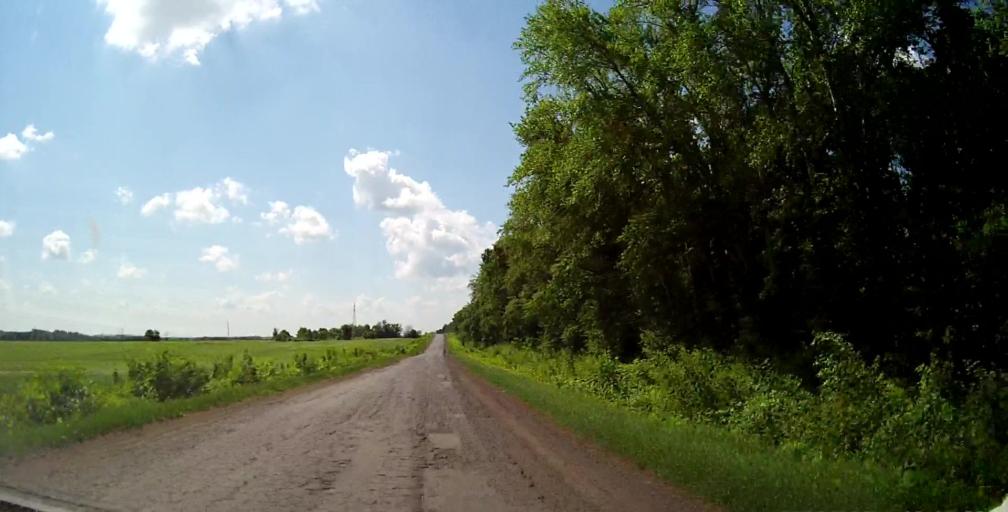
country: RU
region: Lipetsk
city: Chaplygin
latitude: 53.2965
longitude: 39.9552
